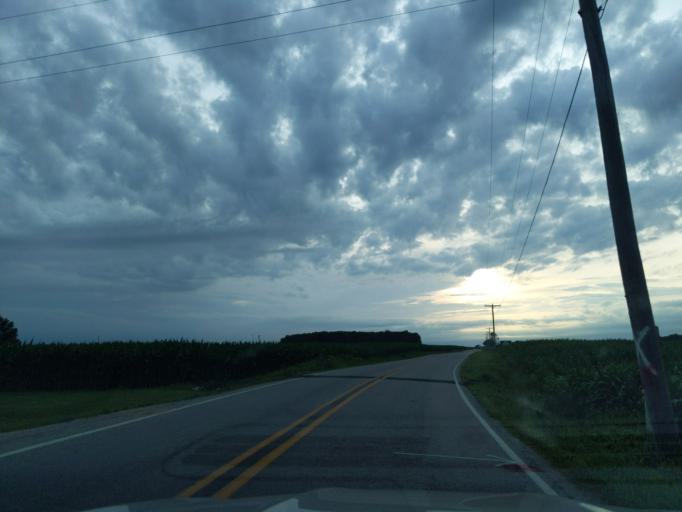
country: US
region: Indiana
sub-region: Ripley County
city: Osgood
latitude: 39.1988
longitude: -85.3018
